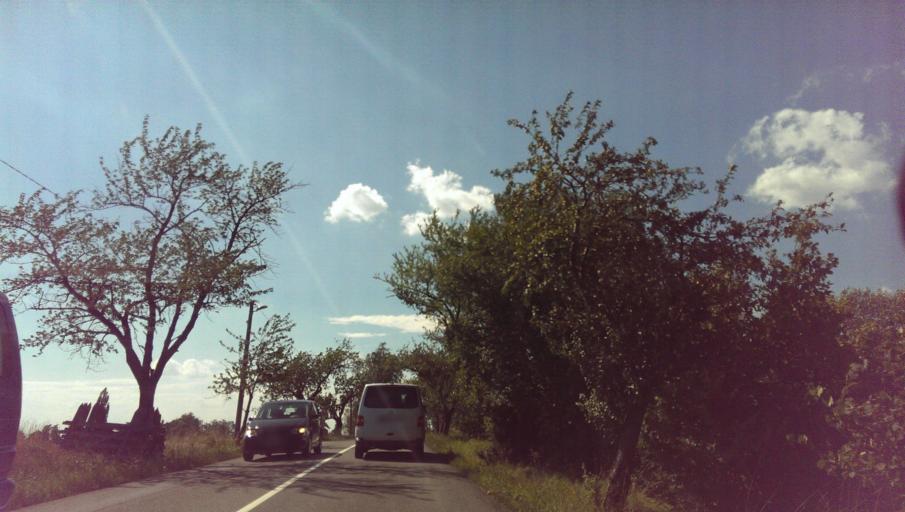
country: CZ
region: Zlin
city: Kelc
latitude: 49.4423
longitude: 17.8267
